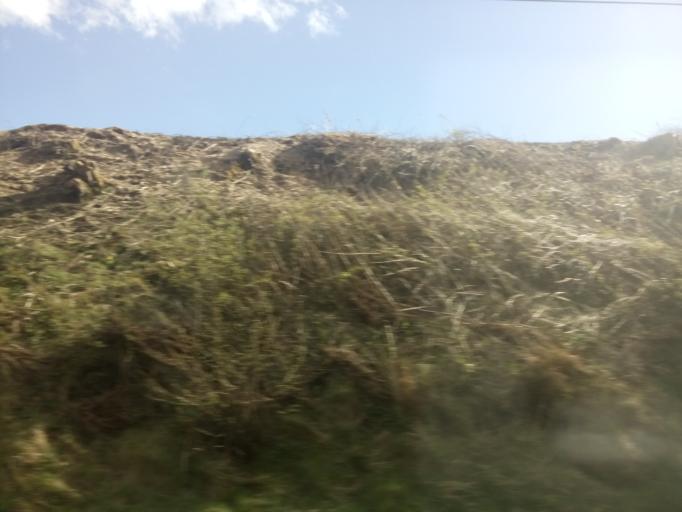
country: GB
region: England
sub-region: County Durham
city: Spennymoor
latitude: 54.7291
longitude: -1.5784
